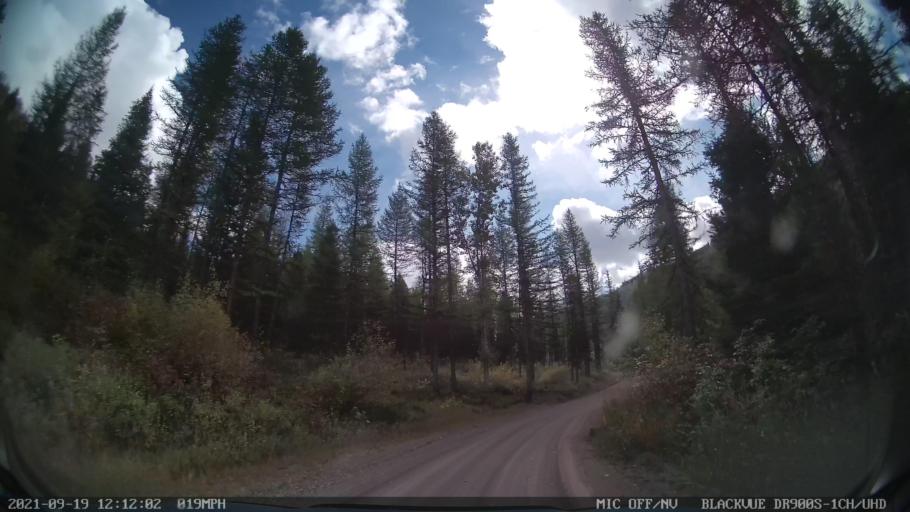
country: US
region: Montana
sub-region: Missoula County
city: Seeley Lake
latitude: 47.1729
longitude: -113.3687
